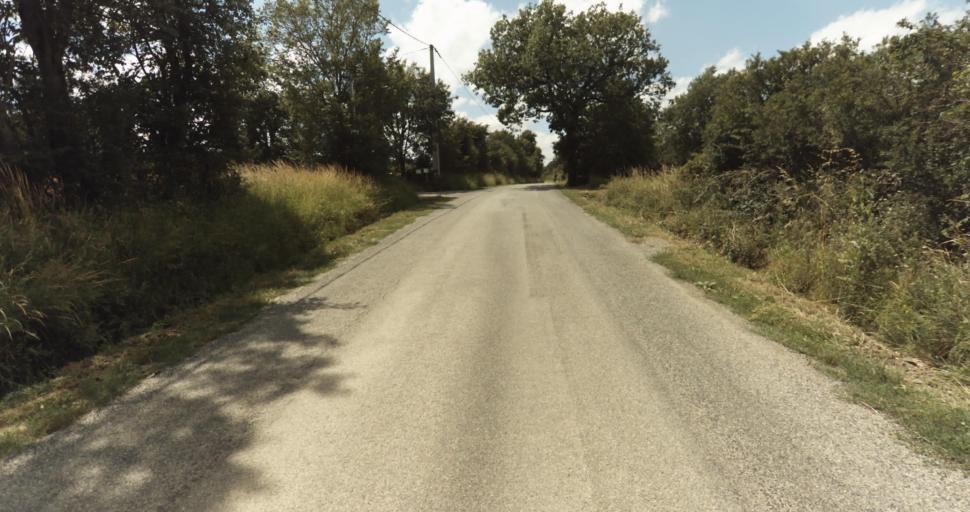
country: FR
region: Midi-Pyrenees
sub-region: Departement de la Haute-Garonne
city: Fontenilles
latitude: 43.5610
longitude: 1.1654
